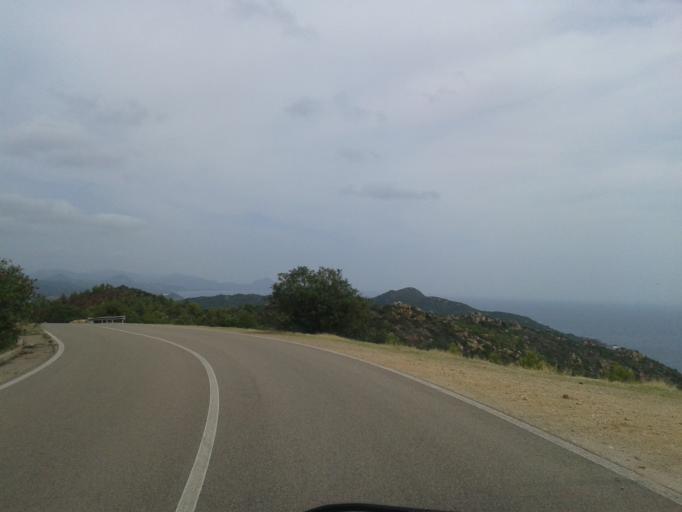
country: IT
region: Sardinia
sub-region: Provincia di Cagliari
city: Villasimius
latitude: 39.1610
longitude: 9.5632
